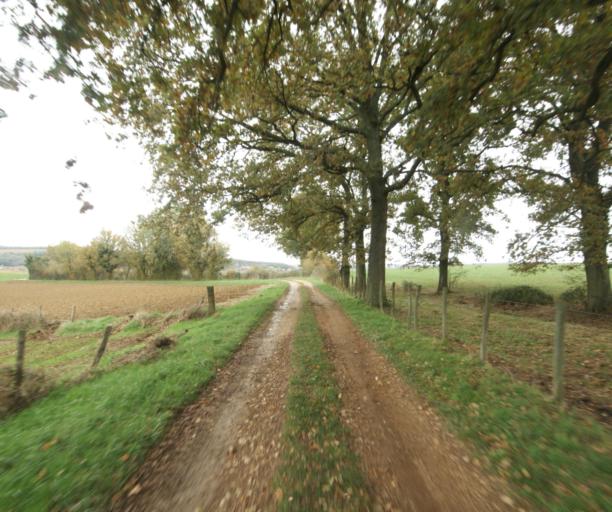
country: FR
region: Rhone-Alpes
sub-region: Departement de l'Ain
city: Pont-de-Vaux
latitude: 46.4625
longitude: 4.8701
